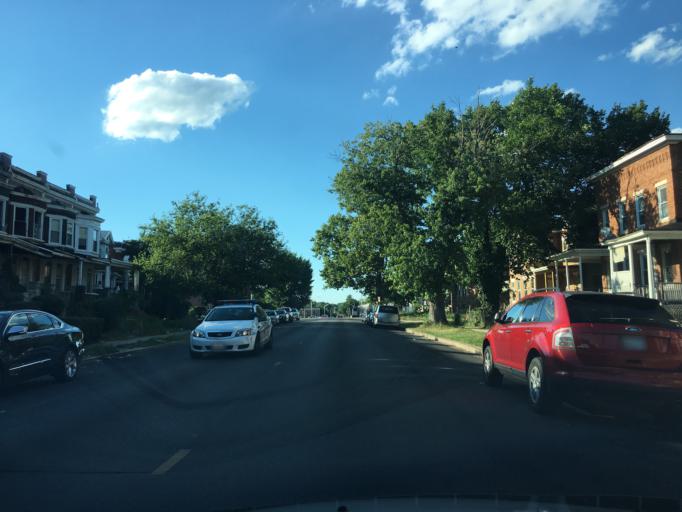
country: US
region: Maryland
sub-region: Baltimore County
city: Charlestown
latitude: 39.2993
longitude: -76.6652
